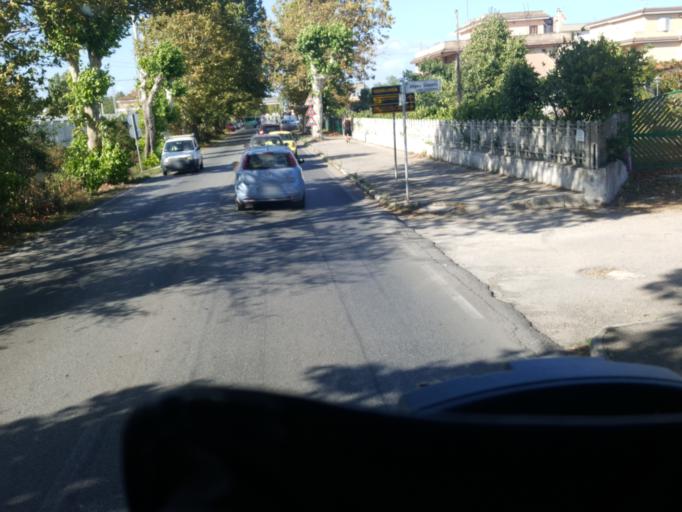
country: IT
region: Latium
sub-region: Provincia di Latina
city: Campo di Carne
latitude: 41.5503
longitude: 12.6353
